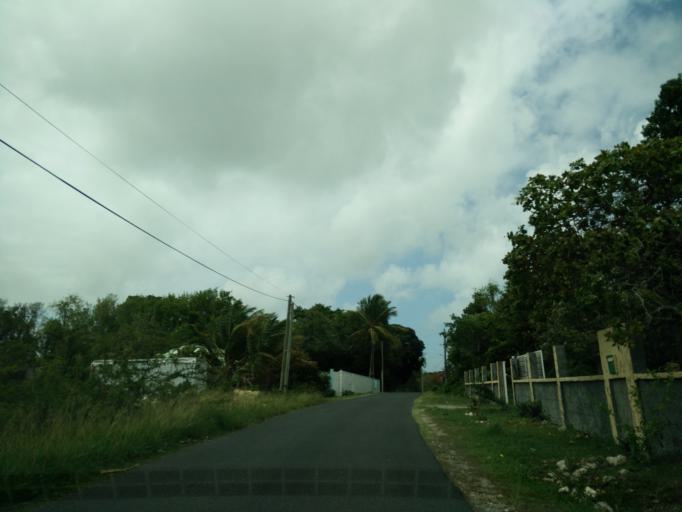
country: GP
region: Guadeloupe
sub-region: Guadeloupe
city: Grand-Bourg
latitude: 15.9102
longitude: -61.2760
